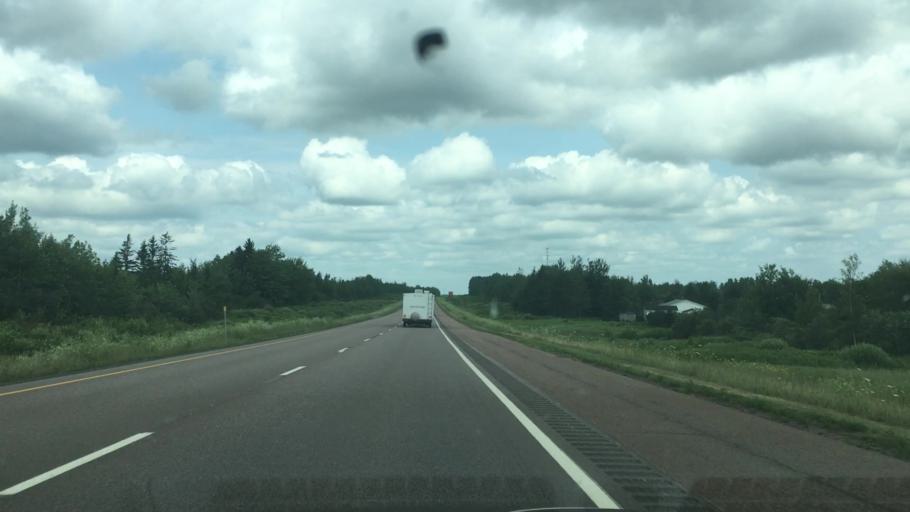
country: CA
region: New Brunswick
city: Dieppe
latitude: 46.0701
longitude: -64.5901
